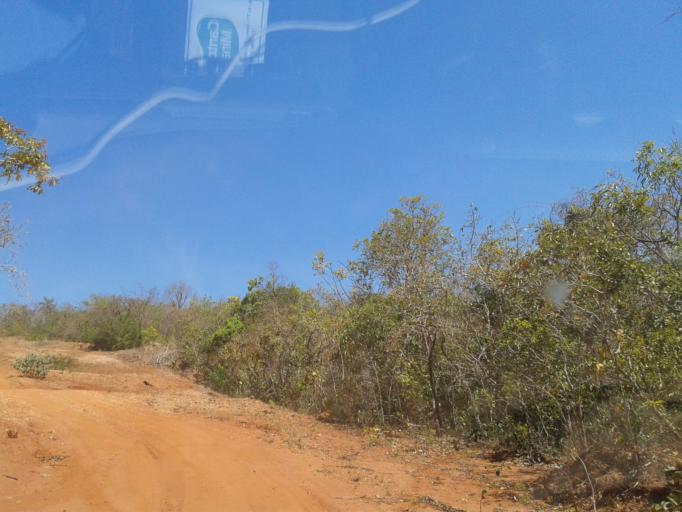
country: BR
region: Minas Gerais
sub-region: Ituiutaba
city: Ituiutaba
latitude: -19.1171
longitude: -49.2934
